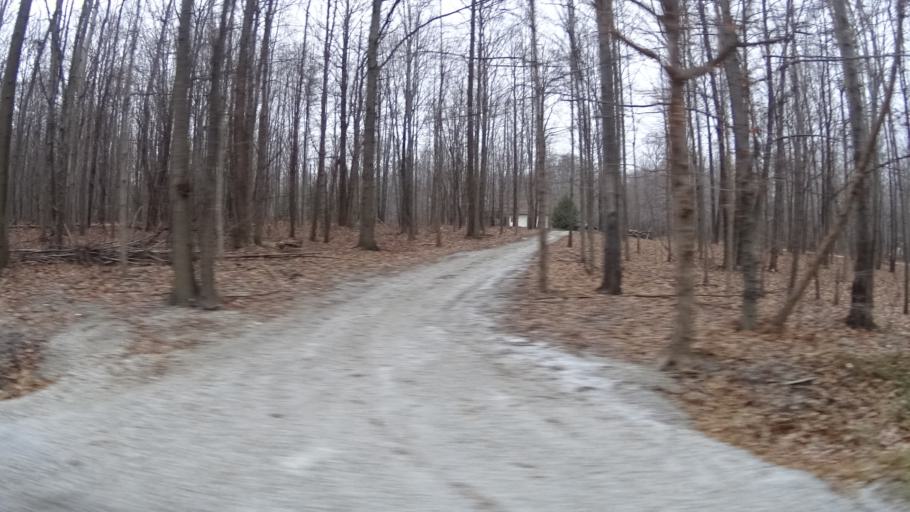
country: US
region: Ohio
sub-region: Lorain County
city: South Amherst
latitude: 41.3385
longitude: -82.2639
